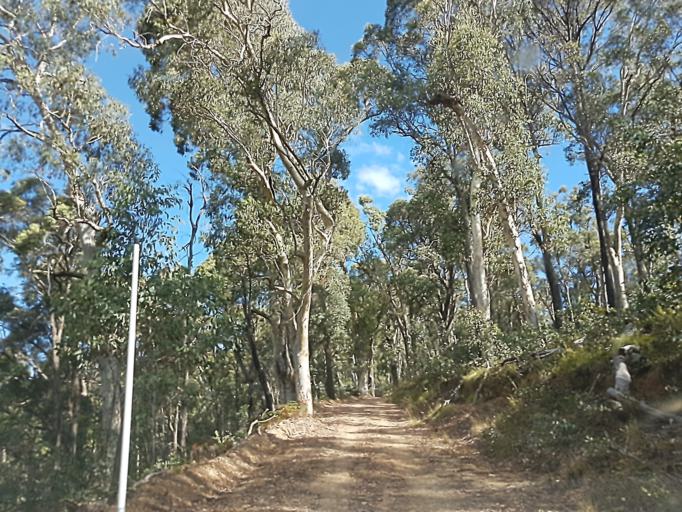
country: AU
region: Victoria
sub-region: Alpine
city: Mount Beauty
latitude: -36.9285
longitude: 146.9944
